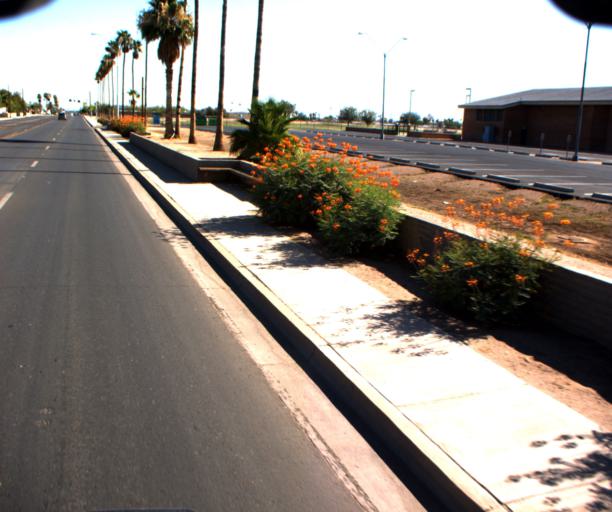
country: US
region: Arizona
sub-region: Pinal County
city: Casa Grande
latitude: 32.8873
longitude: -111.7572
